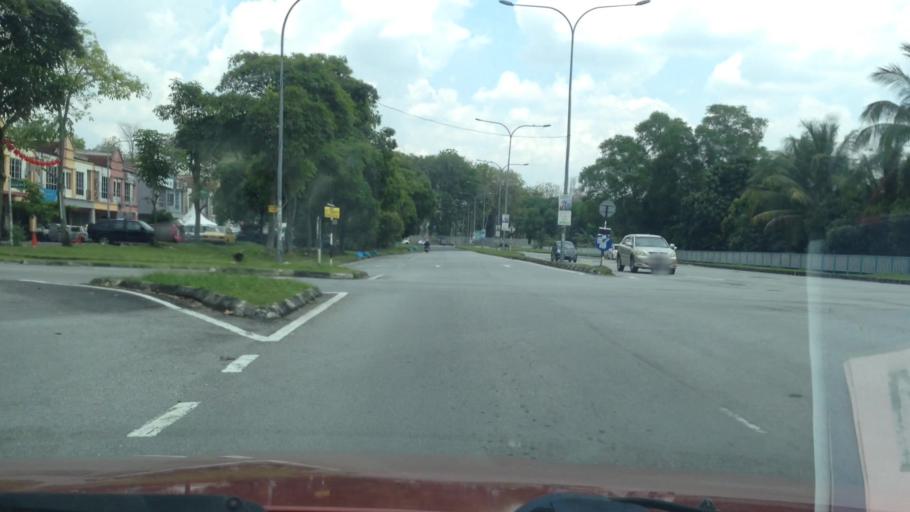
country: MY
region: Selangor
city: Kampung Baru Subang
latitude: 3.1657
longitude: 101.5493
